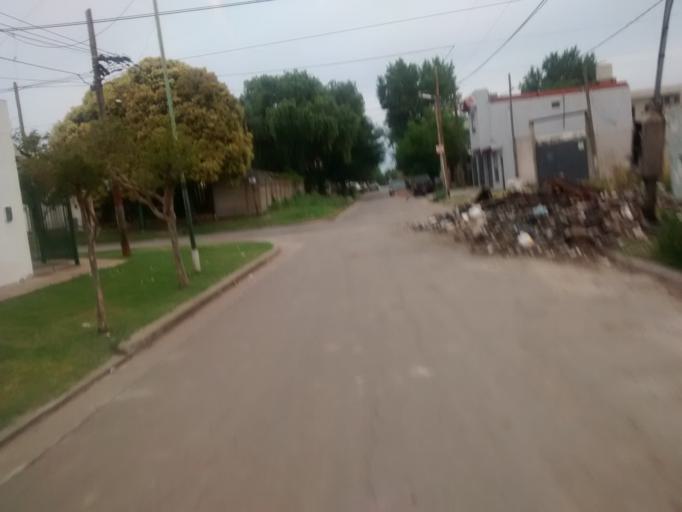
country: AR
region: Buenos Aires
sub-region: Partido de La Plata
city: La Plata
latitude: -34.9442
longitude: -57.9290
